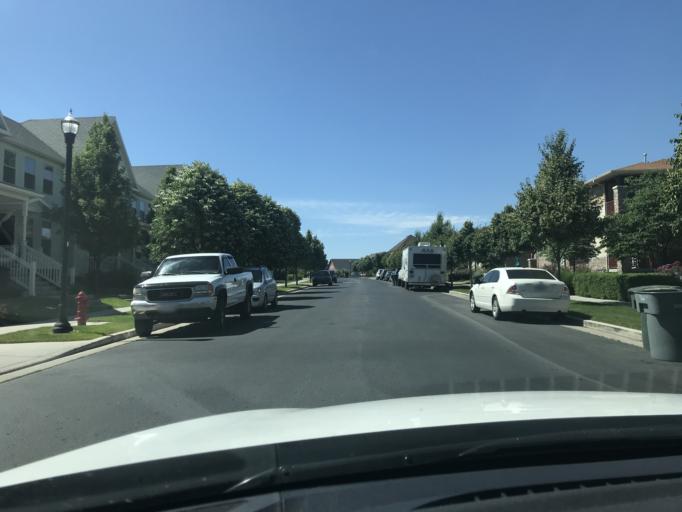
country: US
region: Utah
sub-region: Salt Lake County
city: South Jordan Heights
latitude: 40.5574
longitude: -111.9975
